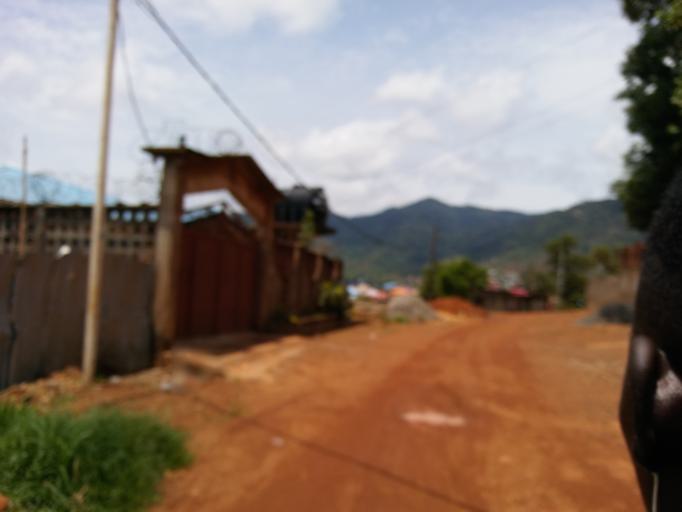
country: SL
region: Western Area
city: Hastings
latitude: 8.3859
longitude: -13.1547
